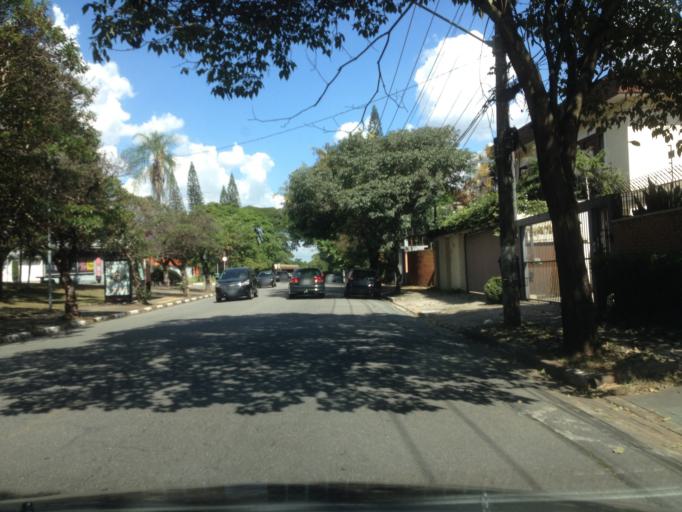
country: BR
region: Sao Paulo
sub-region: Sao Paulo
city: Sao Paulo
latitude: -23.5471
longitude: -46.7059
